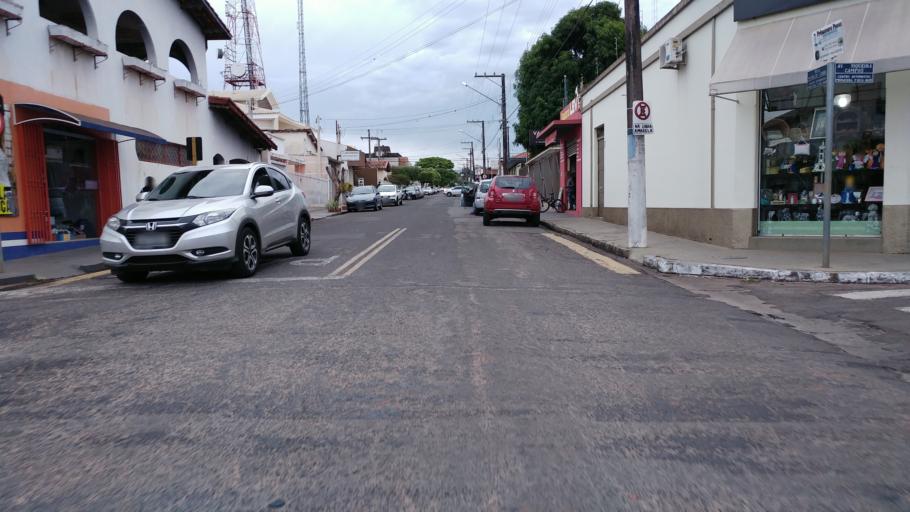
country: BR
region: Sao Paulo
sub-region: Paraguacu Paulista
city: Paraguacu Paulista
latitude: -22.4154
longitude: -50.5773
